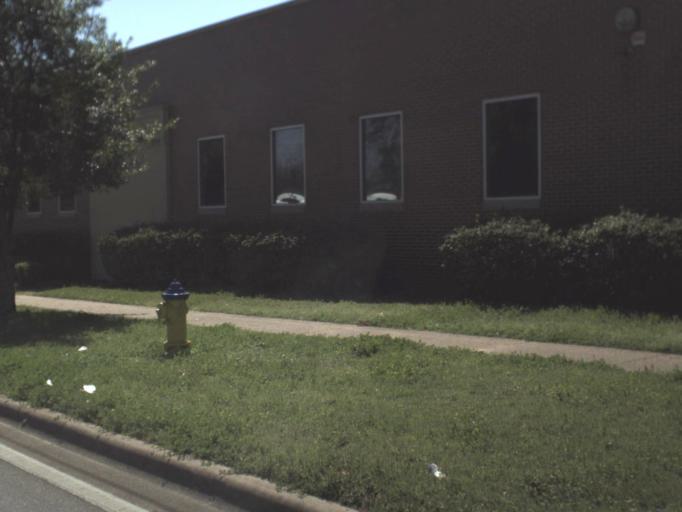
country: US
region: Florida
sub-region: Leon County
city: Tallahassee
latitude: 30.4220
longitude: -84.3024
